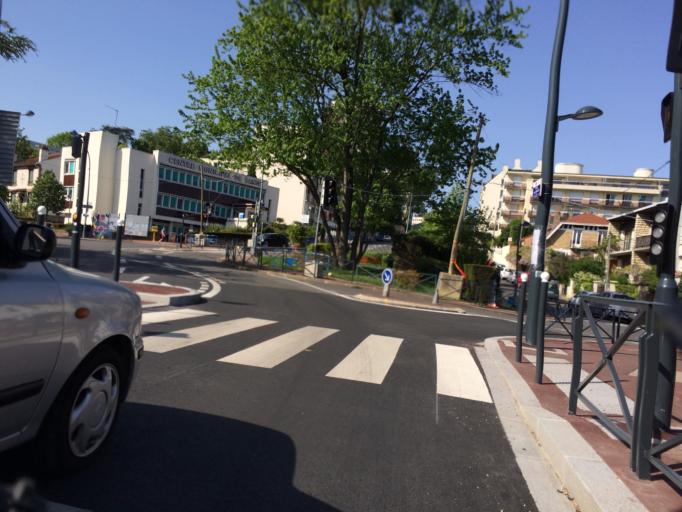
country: FR
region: Ile-de-France
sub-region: Departement des Hauts-de-Seine
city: Fontenay-aux-Roses
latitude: 48.7885
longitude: 2.2881
